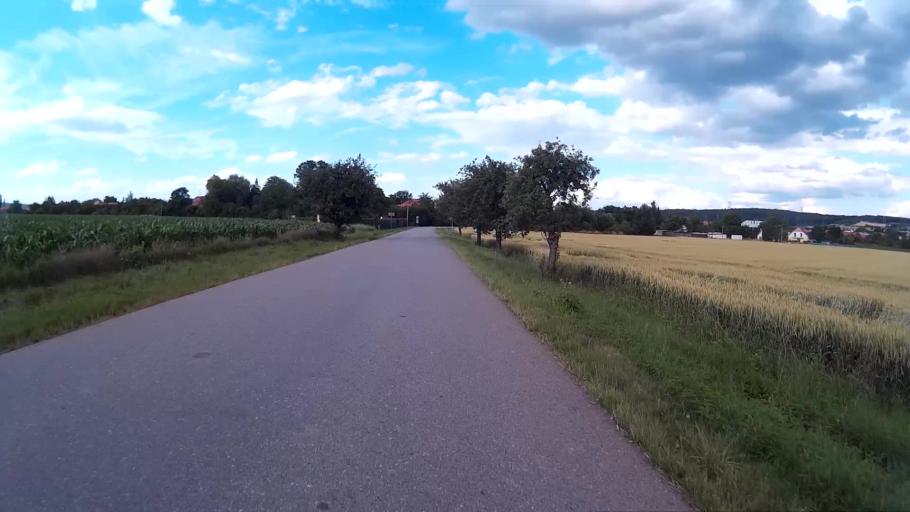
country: CZ
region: South Moravian
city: Ricany
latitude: 49.2079
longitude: 16.4068
